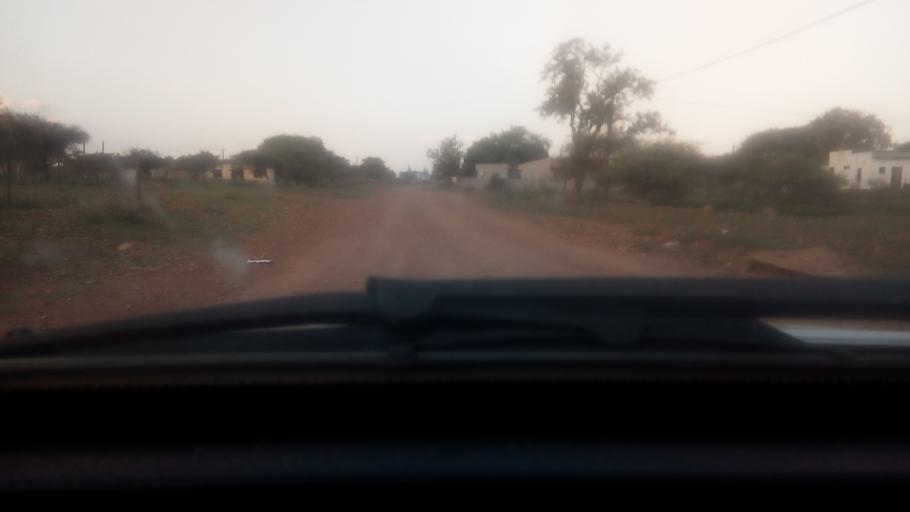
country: BW
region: Kgatleng
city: Bokaa
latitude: -24.4282
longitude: 26.0148
